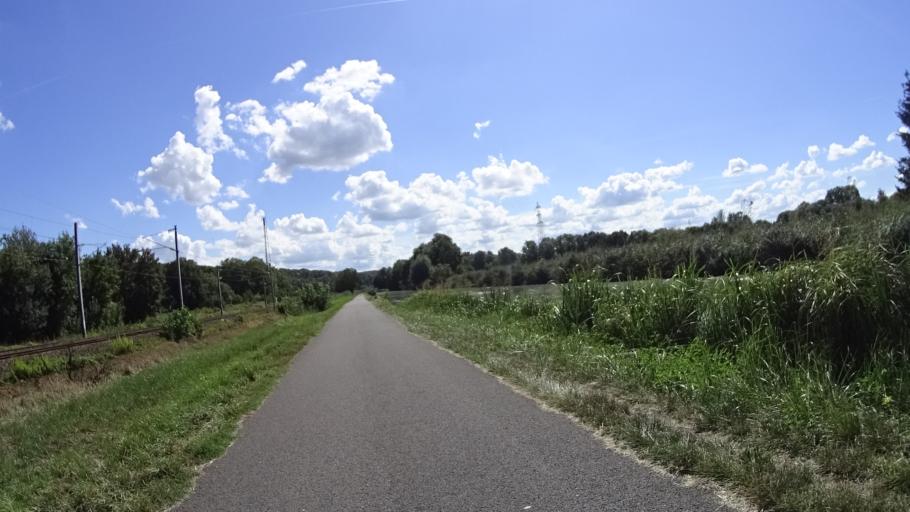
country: FR
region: Alsace
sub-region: Departement du Haut-Rhin
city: Didenheim
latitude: 47.7100
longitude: 7.3113
